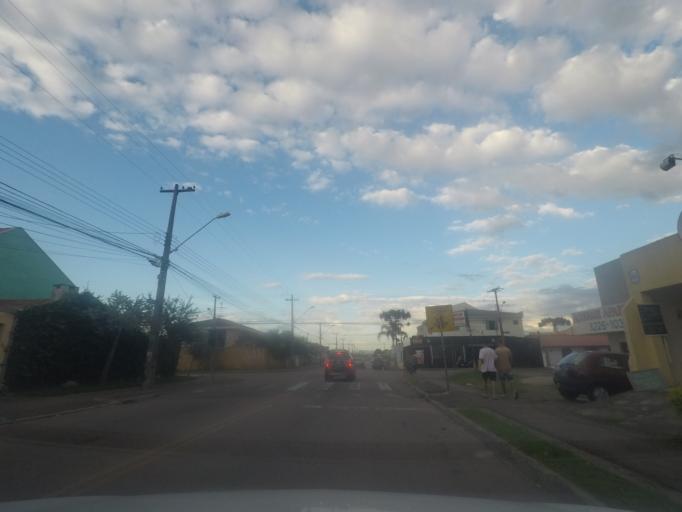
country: BR
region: Parana
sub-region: Pinhais
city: Pinhais
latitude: -25.4669
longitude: -49.2043
